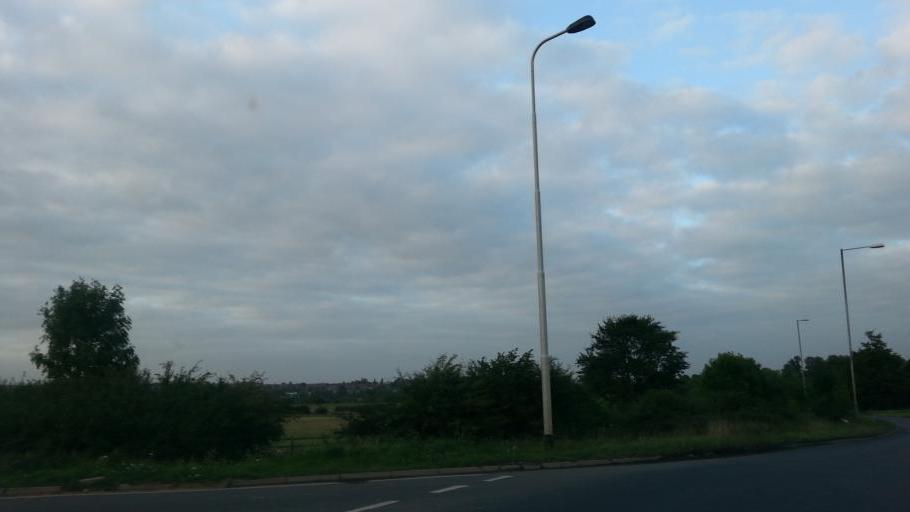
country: GB
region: England
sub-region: Northamptonshire
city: Brackley
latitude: 52.0124
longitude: -1.1576
